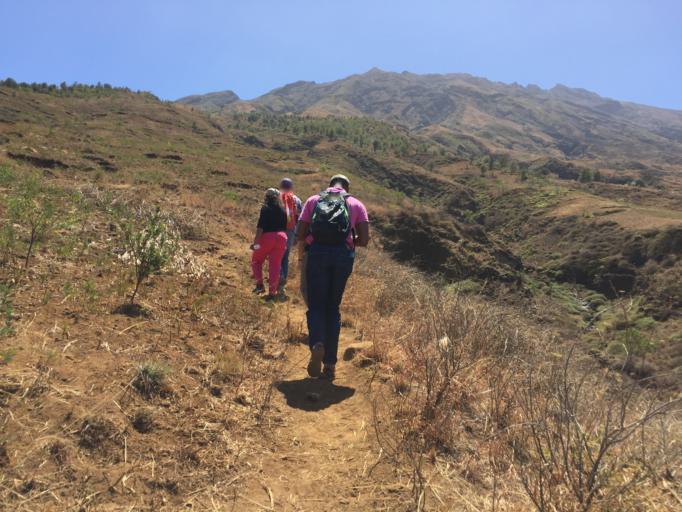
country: CV
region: Mosteiros
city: Porto dos Mosteiros
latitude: 15.0093
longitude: -24.3855
